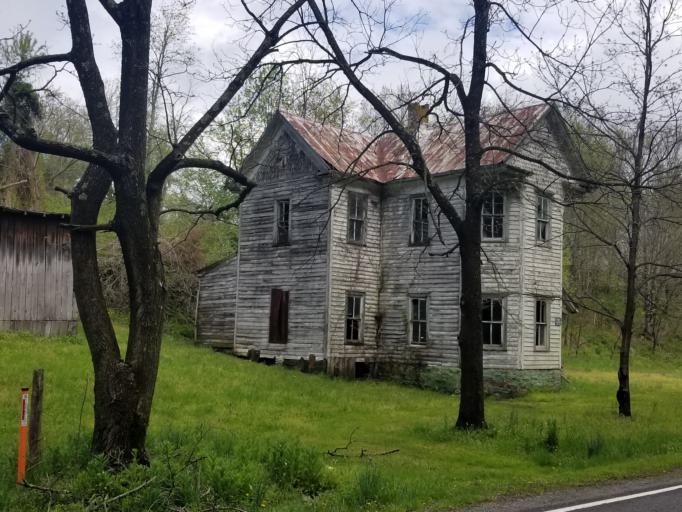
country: US
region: Virginia
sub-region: Wythe County
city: Rural Retreat
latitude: 37.0166
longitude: -81.3503
